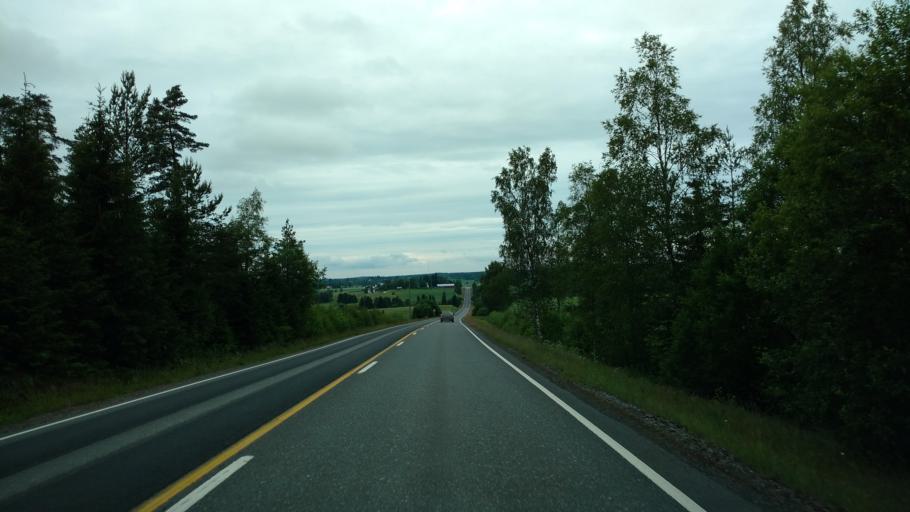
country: FI
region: Varsinais-Suomi
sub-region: Salo
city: Halikko
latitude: 60.4644
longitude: 23.0183
